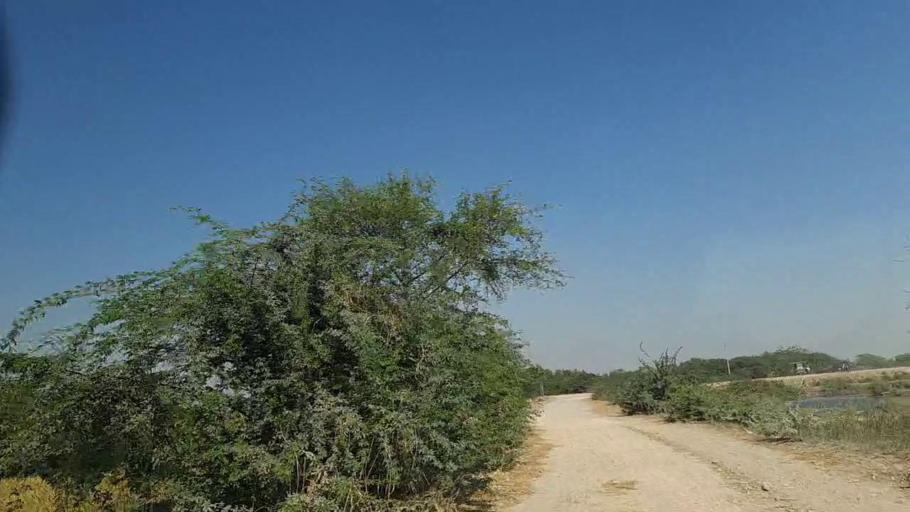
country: PK
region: Sindh
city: Mirpur Batoro
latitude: 24.7373
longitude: 68.2522
